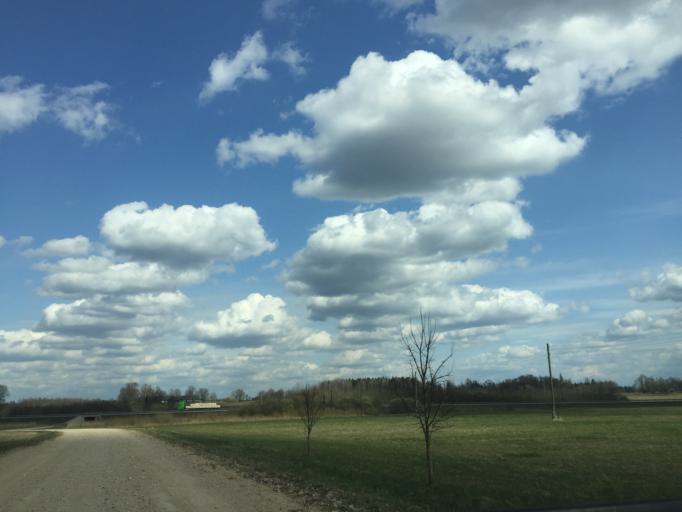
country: LV
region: Skriveri
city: Skriveri
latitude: 56.7510
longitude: 25.1147
